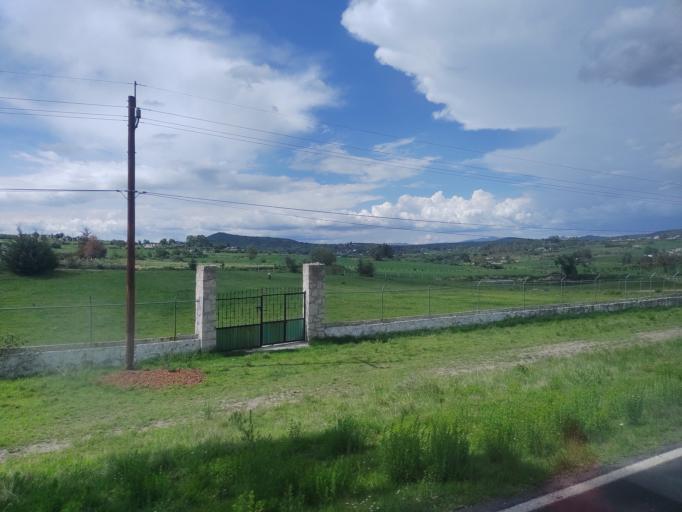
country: MX
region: Mexico
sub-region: Aculco
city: El Colorado
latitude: 20.0967
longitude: -99.7590
